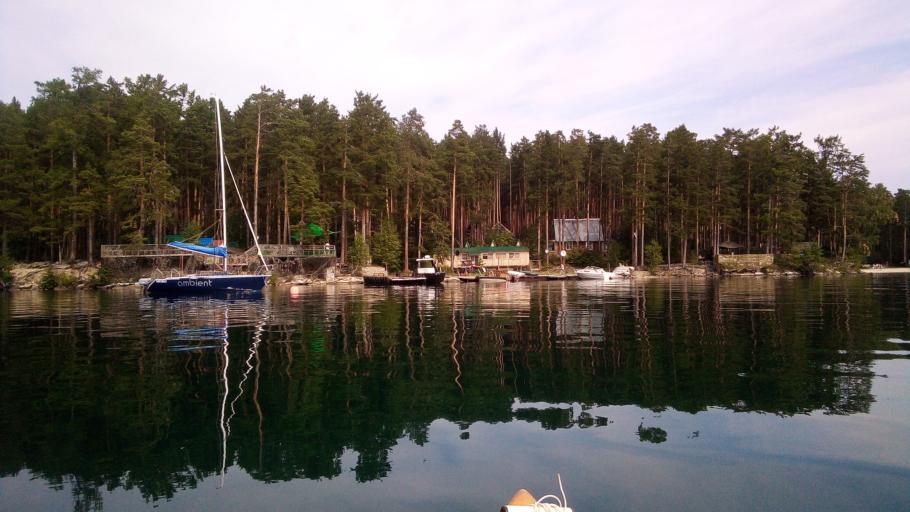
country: RU
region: Chelyabinsk
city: Turgoyak
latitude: 55.1770
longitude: 60.0358
